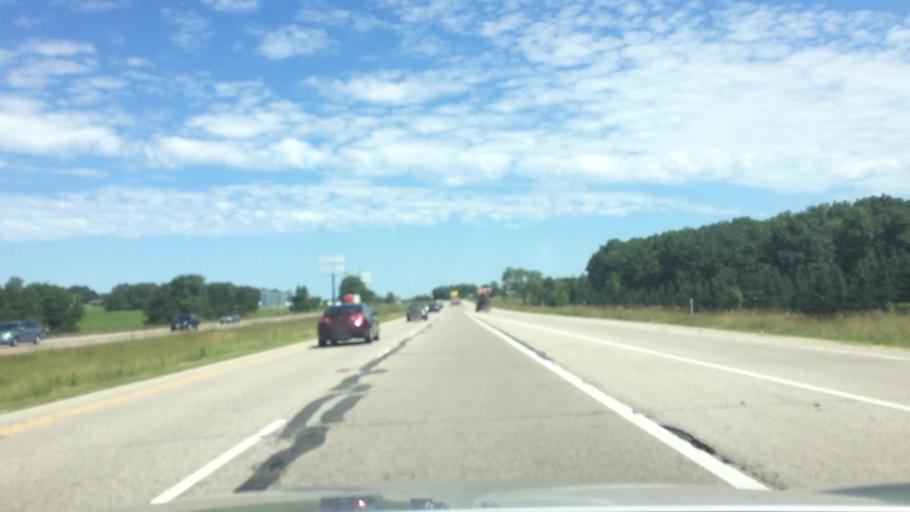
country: US
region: Wisconsin
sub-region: Columbia County
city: Portage
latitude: 43.7038
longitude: -89.4716
